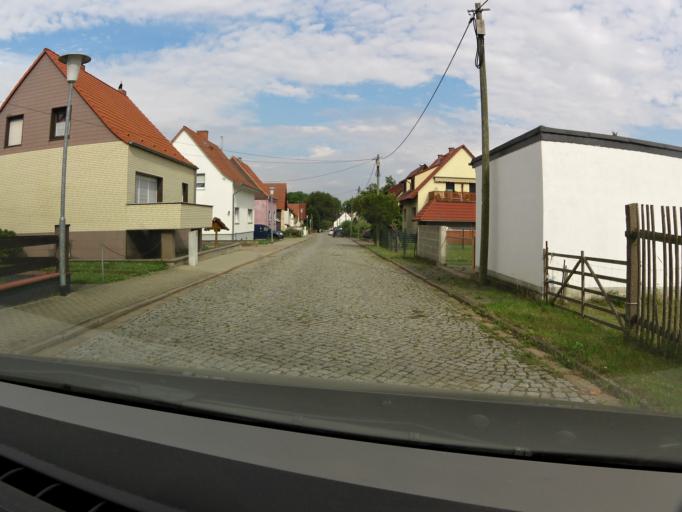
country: DE
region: Thuringia
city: Haina
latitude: 51.0073
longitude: 10.4902
